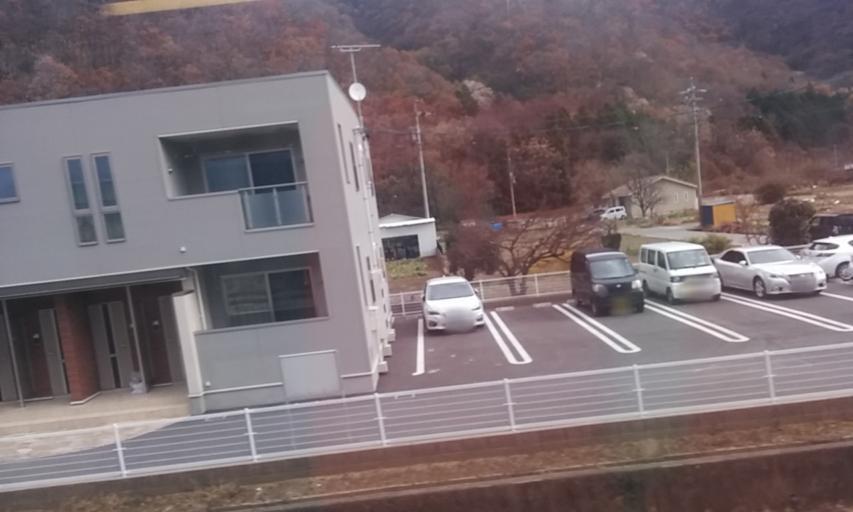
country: JP
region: Nagano
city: Nagano-shi
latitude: 36.5105
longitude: 138.1402
